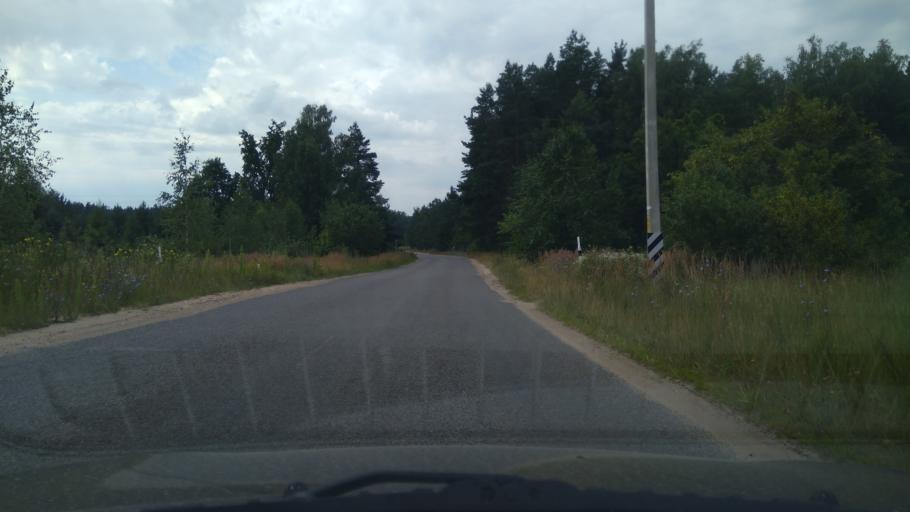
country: BY
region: Brest
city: Nyakhachava
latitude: 52.6076
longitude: 25.0861
